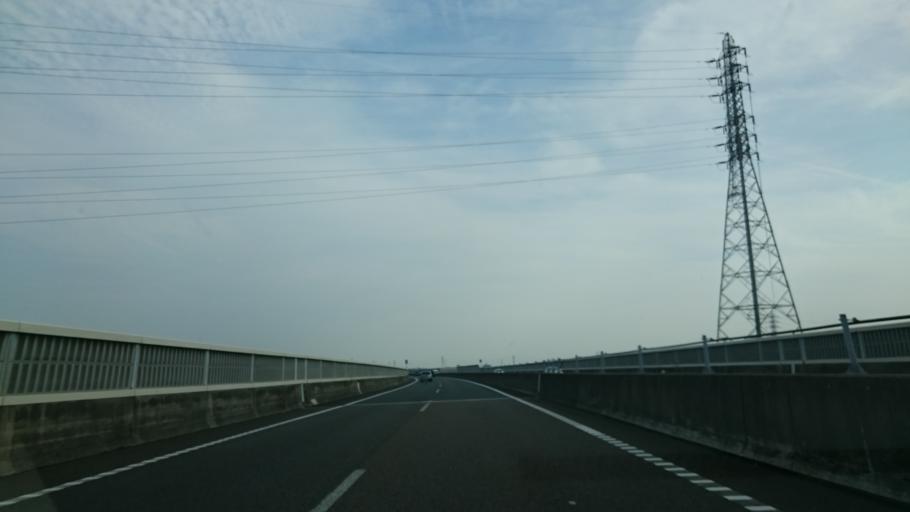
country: JP
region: Aichi
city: Ichinomiya
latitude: 35.3130
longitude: 136.7754
